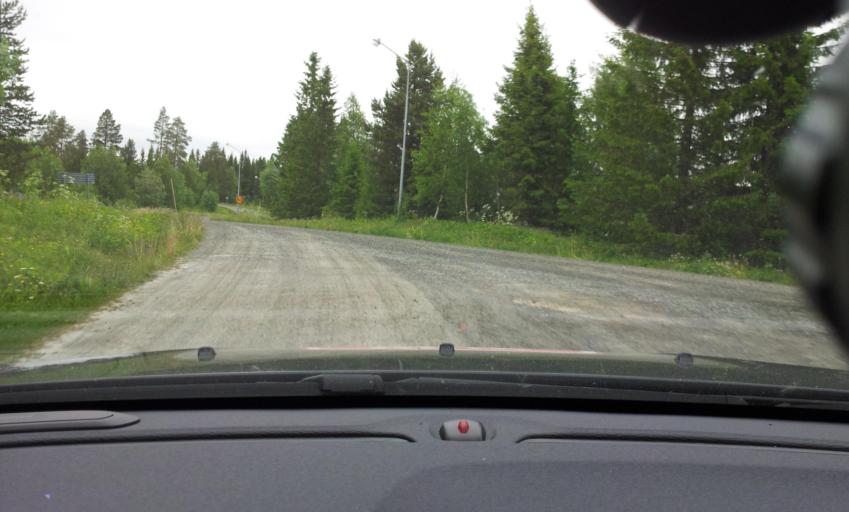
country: SE
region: Jaemtland
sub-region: Are Kommun
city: Jarpen
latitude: 63.2335
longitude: 13.6773
